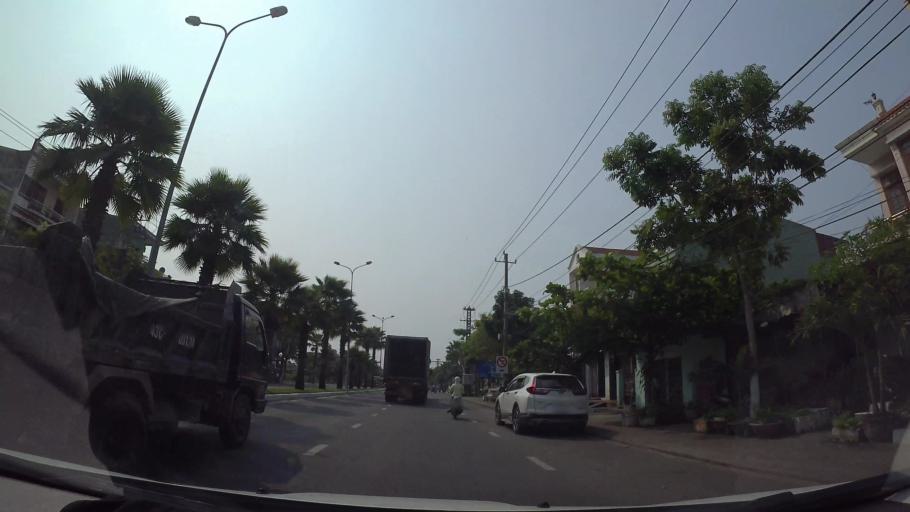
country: VN
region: Da Nang
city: Da Nang
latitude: 16.1065
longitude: 108.2463
